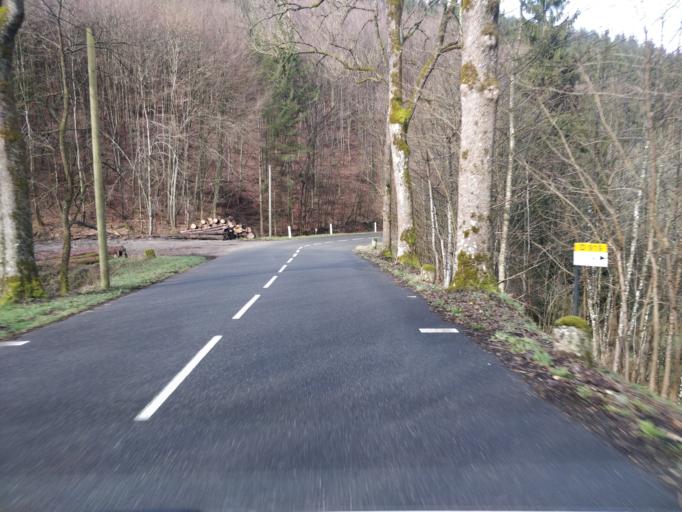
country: FR
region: Lorraine
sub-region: Departement de la Moselle
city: Soucht
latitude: 48.9193
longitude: 7.3061
